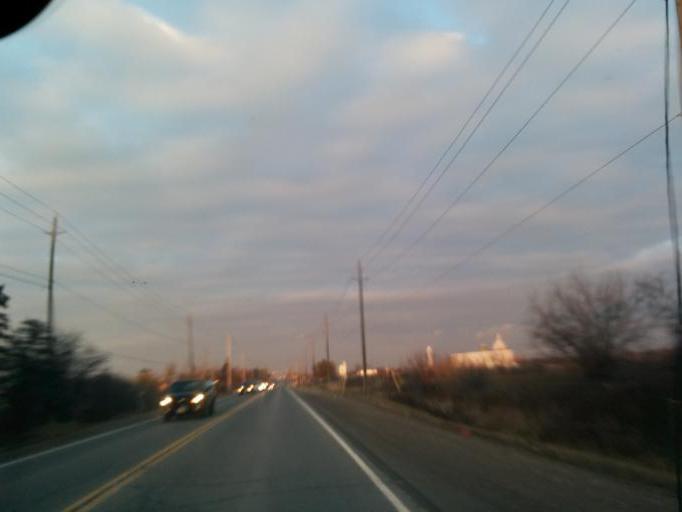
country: CA
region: Ontario
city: Brampton
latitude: 43.8249
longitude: -79.7215
